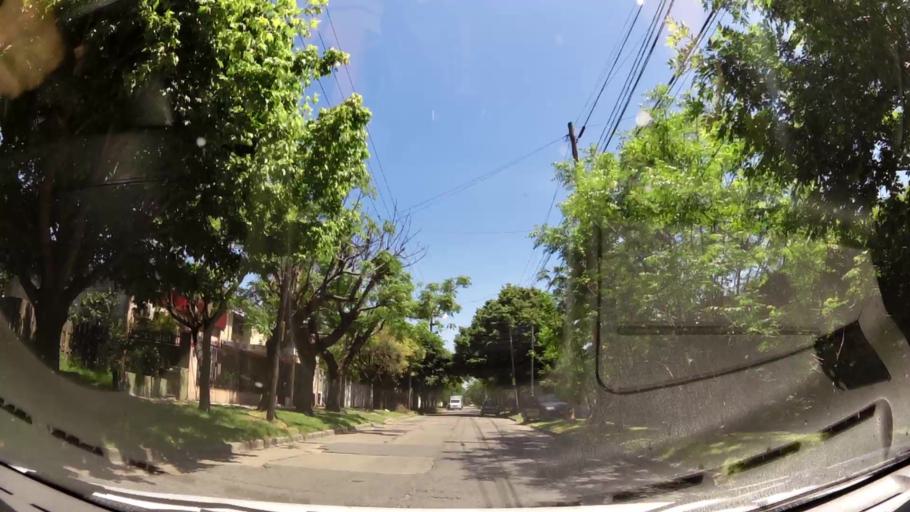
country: AR
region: Buenos Aires
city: Ituzaingo
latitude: -34.6565
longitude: -58.6799
